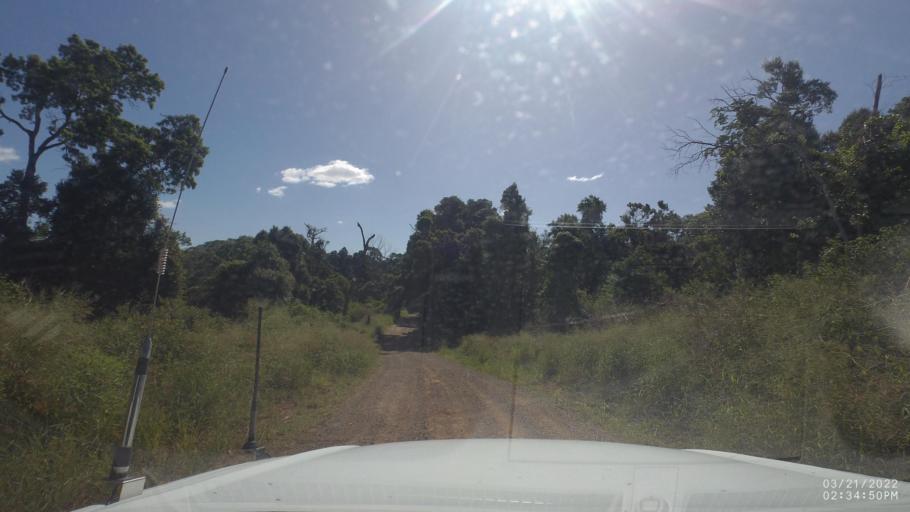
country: AU
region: Queensland
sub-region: Ipswich
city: Deebing Heights
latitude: -27.8290
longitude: 152.8224
